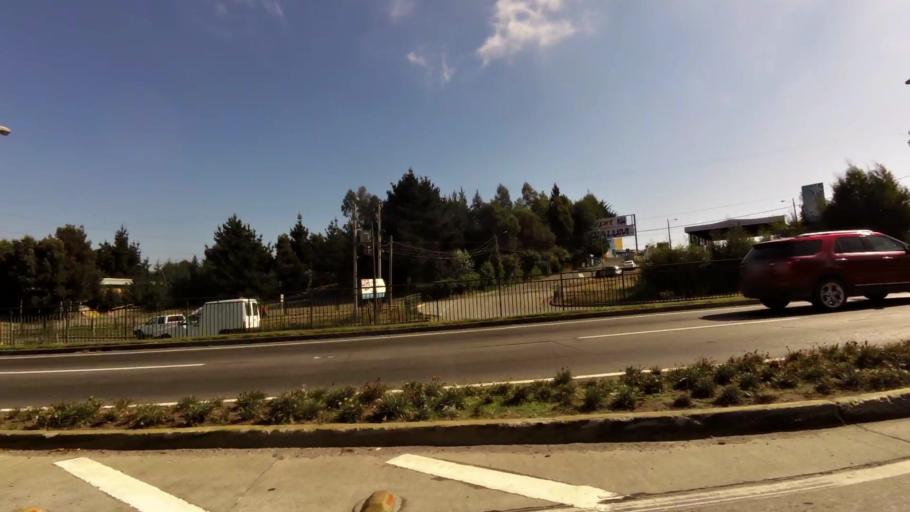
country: CL
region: Biobio
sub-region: Provincia de Concepcion
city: Concepcion
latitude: -36.7983
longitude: -73.0600
